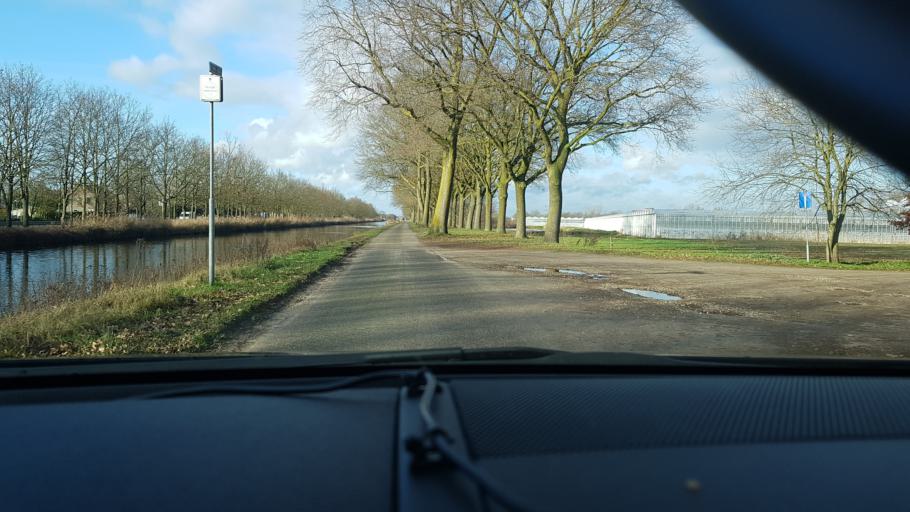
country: NL
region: North Brabant
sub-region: Gemeente Helmond
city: Helmond
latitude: 51.4512
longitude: 5.6805
